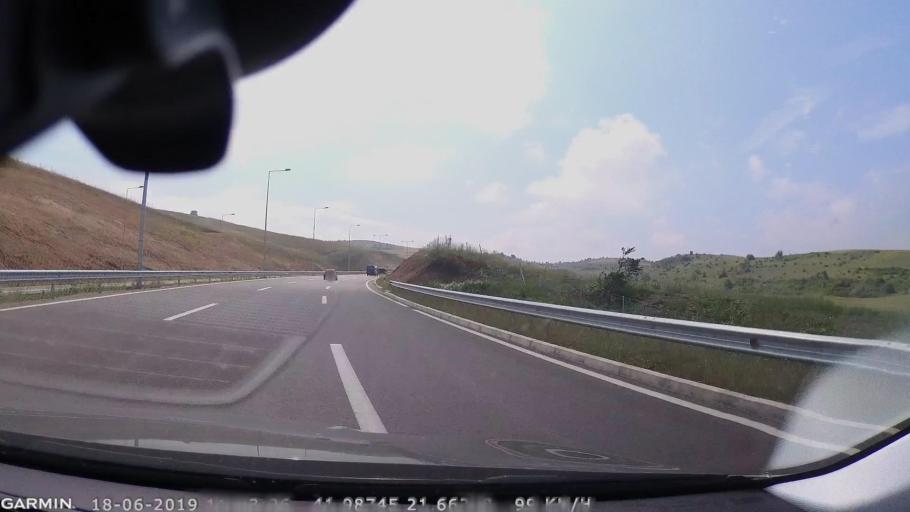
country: MK
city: Miladinovci
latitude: 41.9874
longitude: 21.6632
